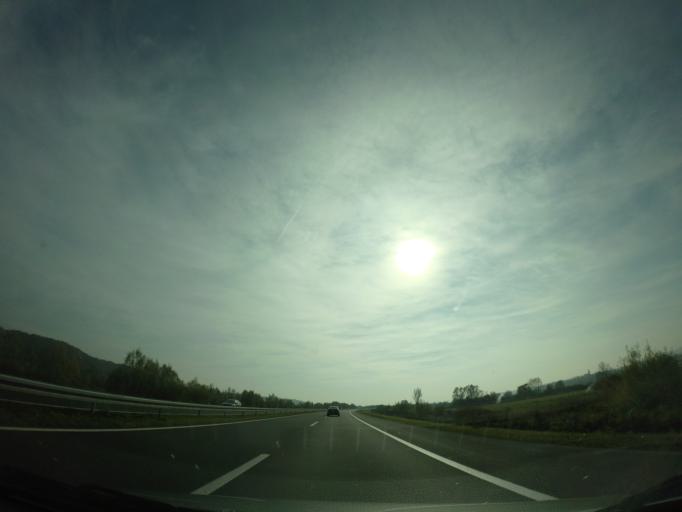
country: HR
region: Varazdinska
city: Remetinec
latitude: 46.0116
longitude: 16.2944
